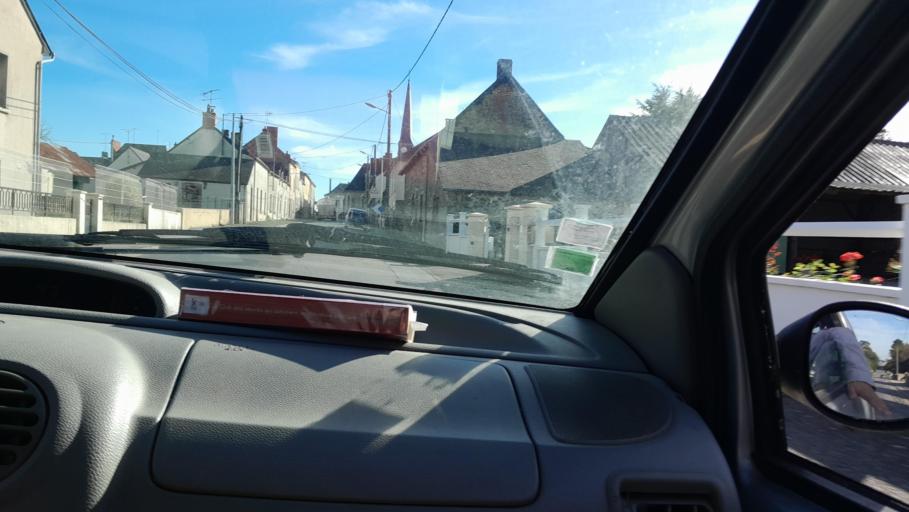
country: FR
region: Brittany
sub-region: Departement d'Ille-et-Vilaine
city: Argentre-du-Plessis
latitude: 47.9719
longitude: -1.1197
